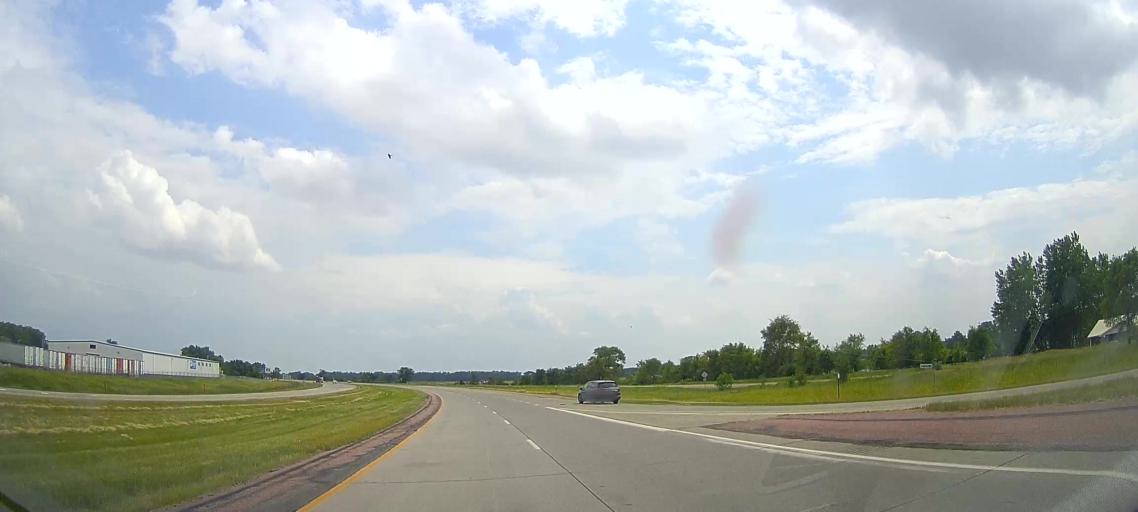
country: US
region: South Dakota
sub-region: Union County
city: Elk Point
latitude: 42.6886
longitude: -96.6973
